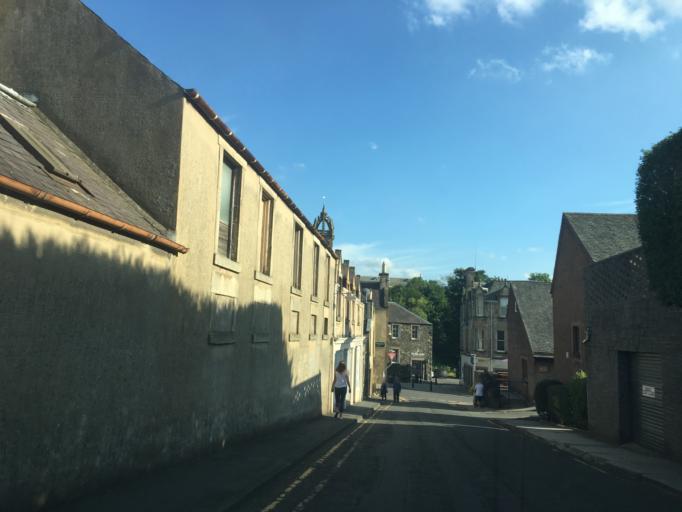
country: GB
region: Scotland
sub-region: The Scottish Borders
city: Peebles
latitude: 55.6527
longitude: -3.1930
